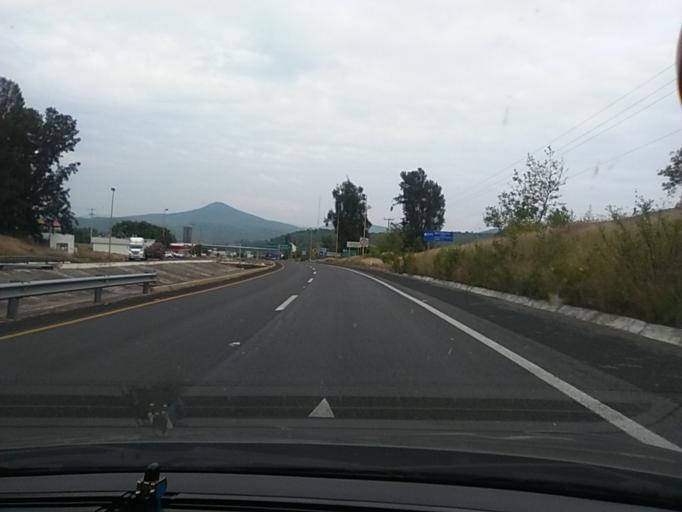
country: MX
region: Michoacan
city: Panindicuaro de la Reforma
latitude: 19.9713
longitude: -101.7607
